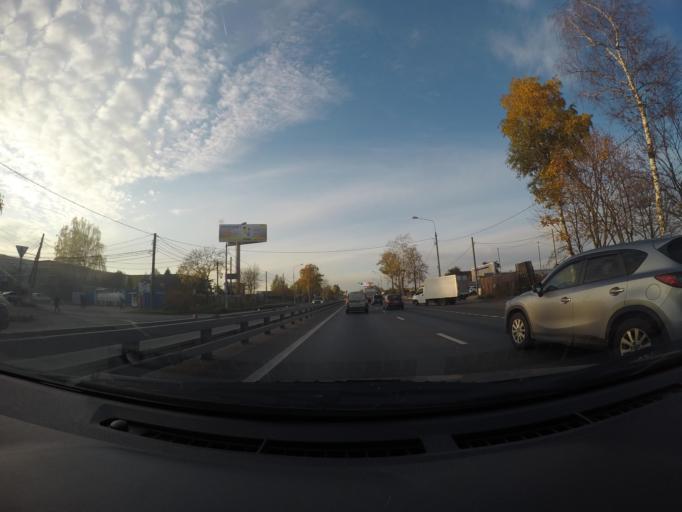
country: RU
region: Moskovskaya
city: Novopodrezkovo
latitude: 55.9592
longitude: 37.3378
